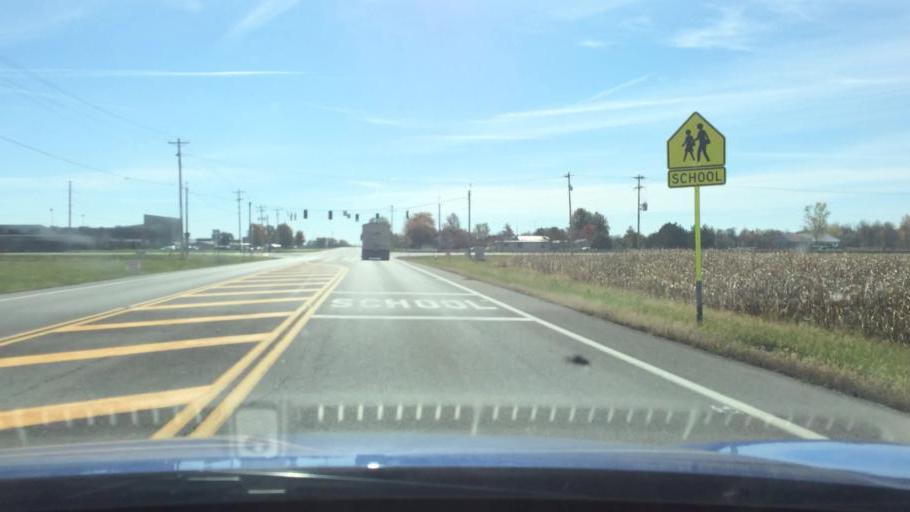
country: US
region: Ohio
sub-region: Logan County
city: Russells Point
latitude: 40.4406
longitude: -83.9061
